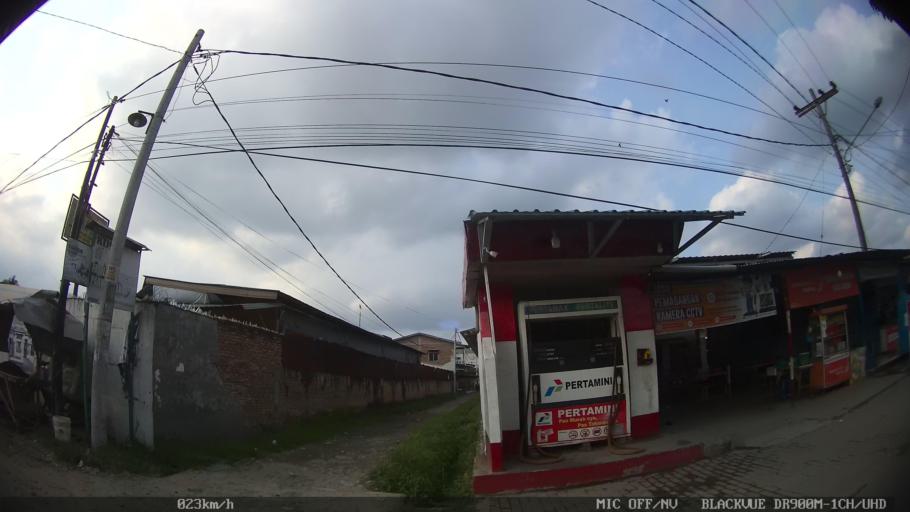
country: ID
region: North Sumatra
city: Medan
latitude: 3.5814
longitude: 98.7365
